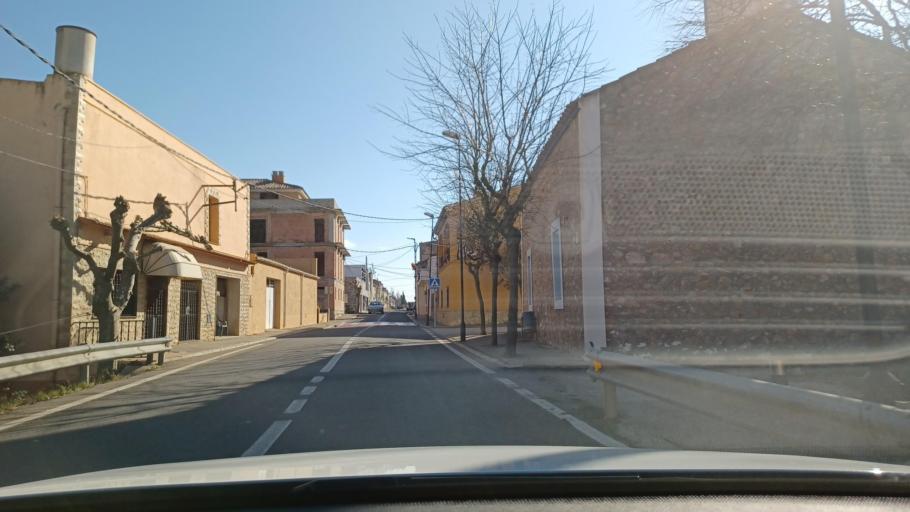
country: ES
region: Catalonia
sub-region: Provincia de Tarragona
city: Ulldecona
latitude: 40.6282
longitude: 0.3649
